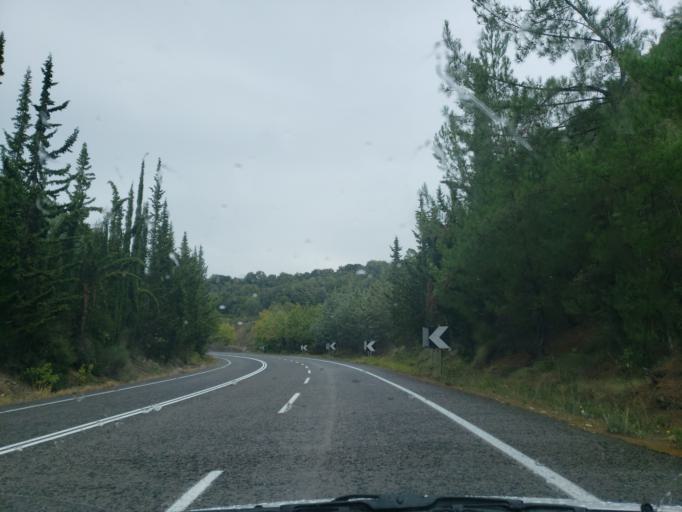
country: GR
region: Central Greece
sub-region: Nomos Fthiotidos
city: Anthili
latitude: 38.7882
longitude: 22.4837
